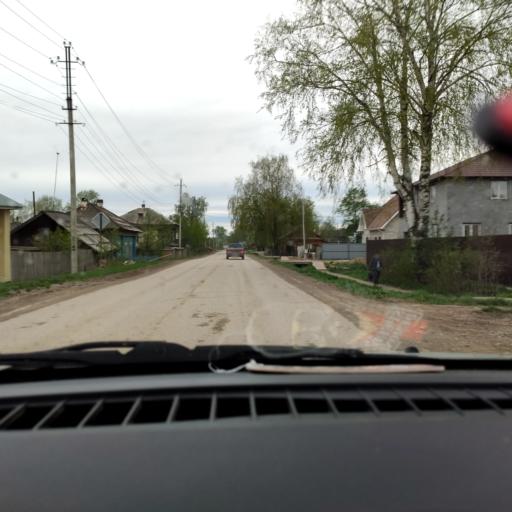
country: RU
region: Perm
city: Kudymkar
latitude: 59.0073
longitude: 54.6597
